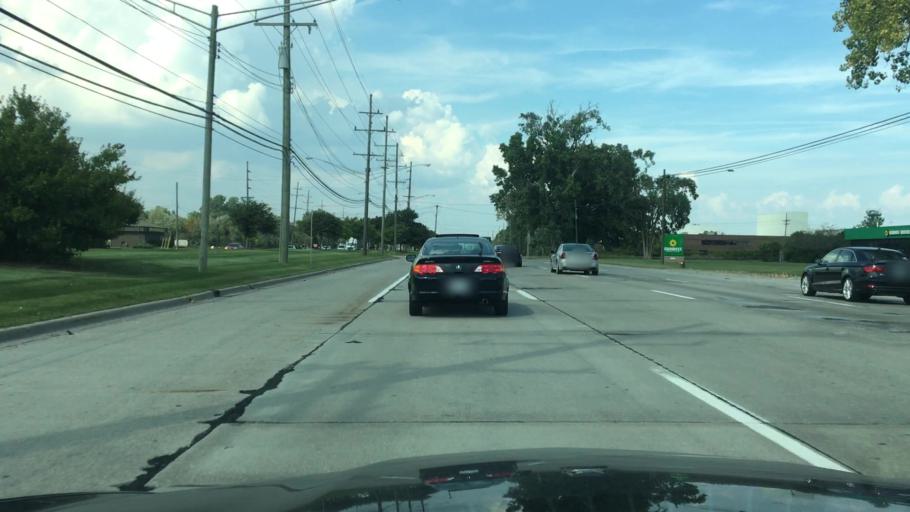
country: US
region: Michigan
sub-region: Macomb County
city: Sterling Heights
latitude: 42.5564
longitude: -83.0486
